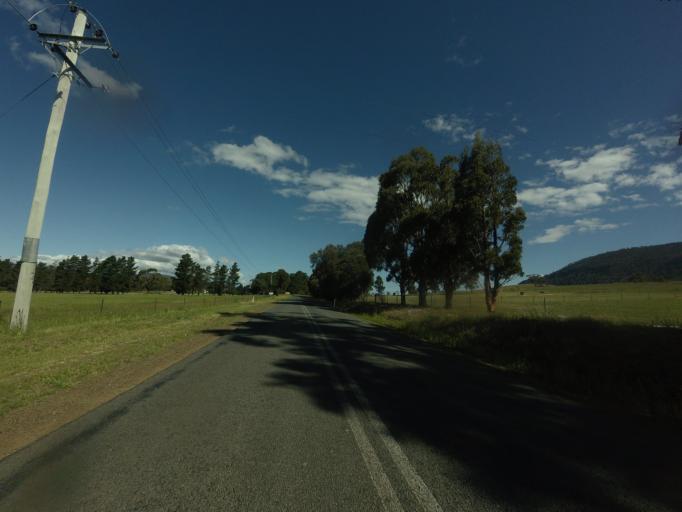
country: AU
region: Tasmania
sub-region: Sorell
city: Sorell
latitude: -42.6114
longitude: 147.4265
